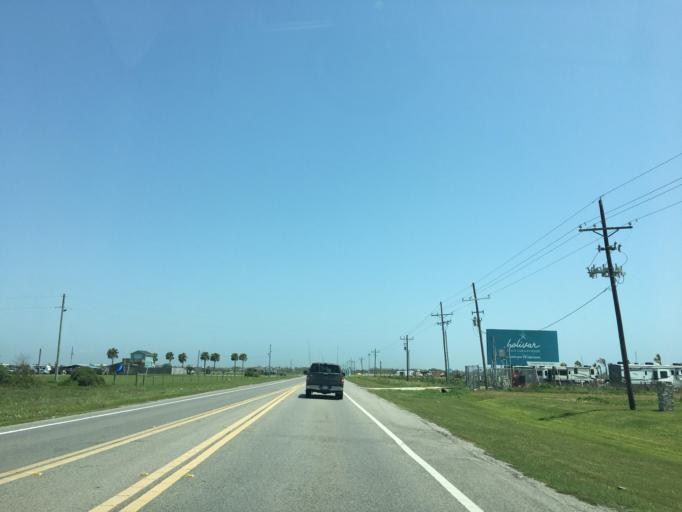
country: US
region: Texas
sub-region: Galveston County
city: Bolivar Peninsula
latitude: 29.4361
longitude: -94.6768
